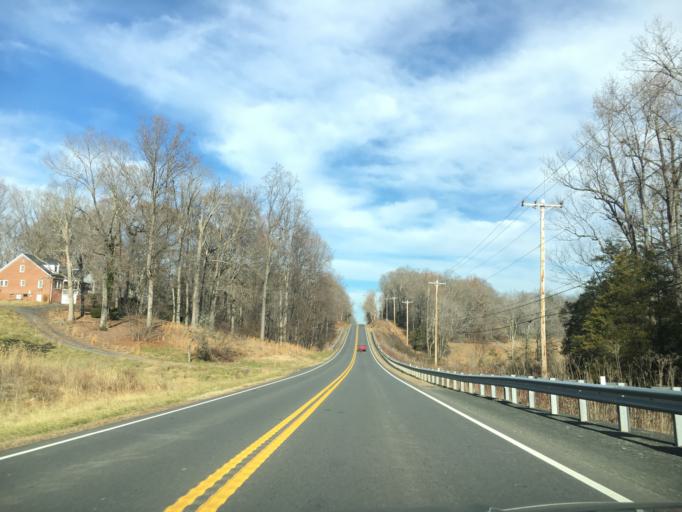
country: US
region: Virginia
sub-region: Fauquier County
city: Warrenton
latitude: 38.6315
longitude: -77.9355
